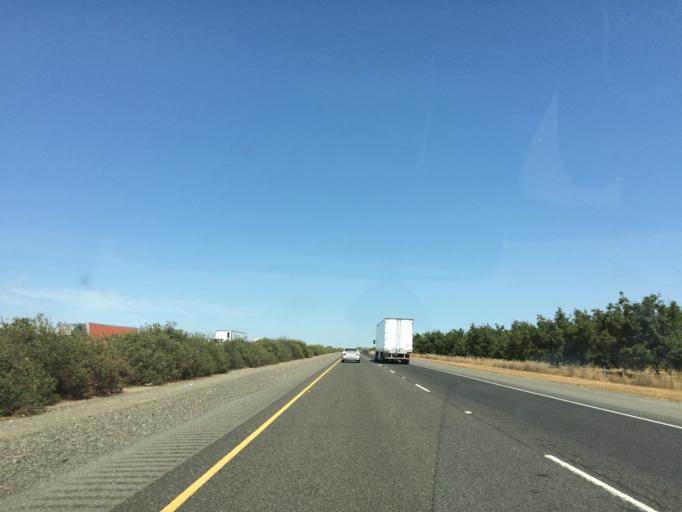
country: US
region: California
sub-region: Glenn County
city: Orland
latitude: 39.6424
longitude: -122.2043
